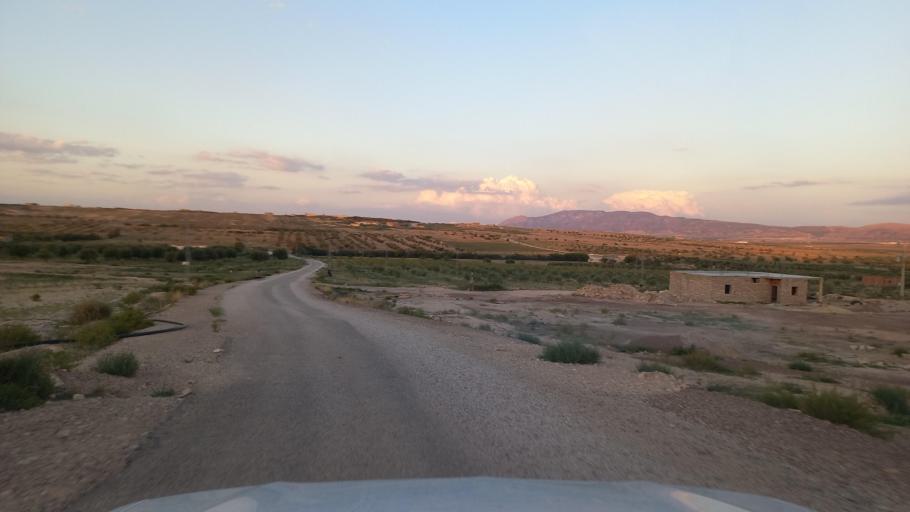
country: TN
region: Al Qasrayn
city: Sbiba
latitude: 35.3724
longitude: 9.0637
